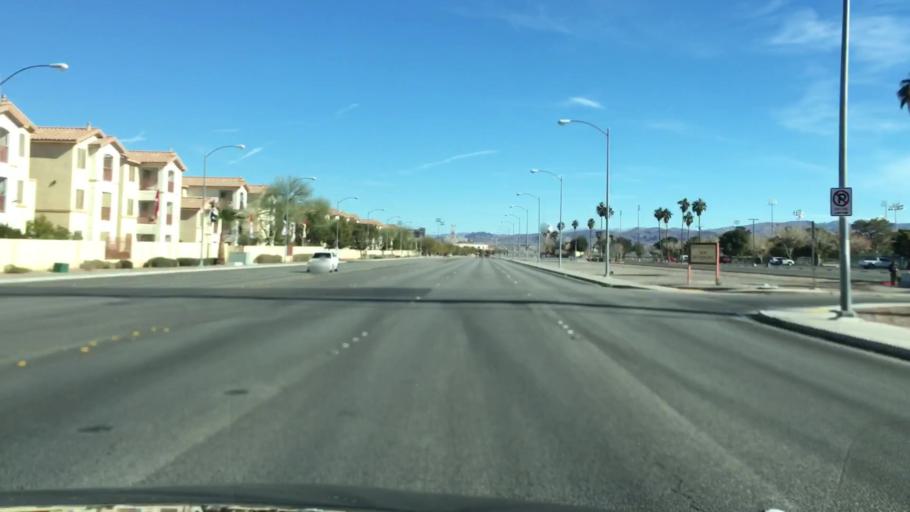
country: US
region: Nevada
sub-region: Clark County
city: Whitney
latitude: 36.0855
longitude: -115.0291
